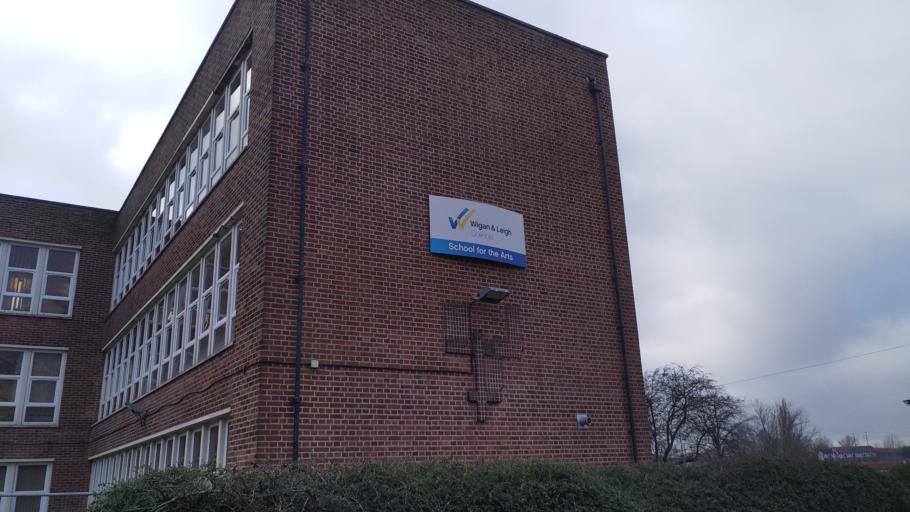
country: GB
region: England
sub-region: Borough of Wigan
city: Ince-in-Makerfield
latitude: 53.5498
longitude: -2.6356
